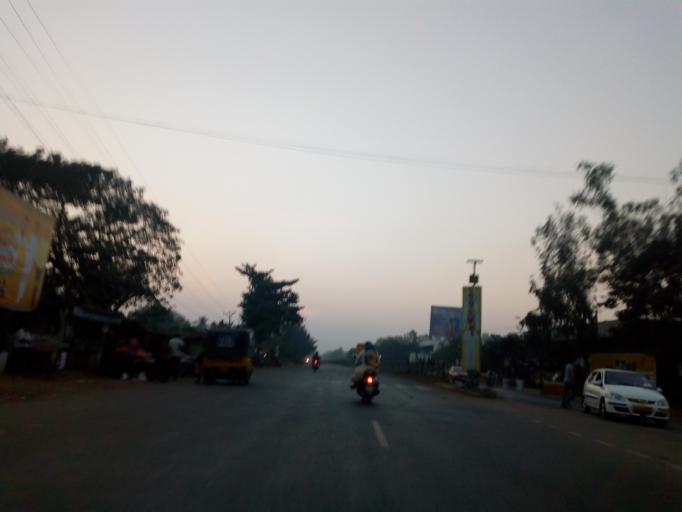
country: IN
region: Andhra Pradesh
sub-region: West Godavari
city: Tadepallegudem
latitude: 16.8235
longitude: 81.4225
